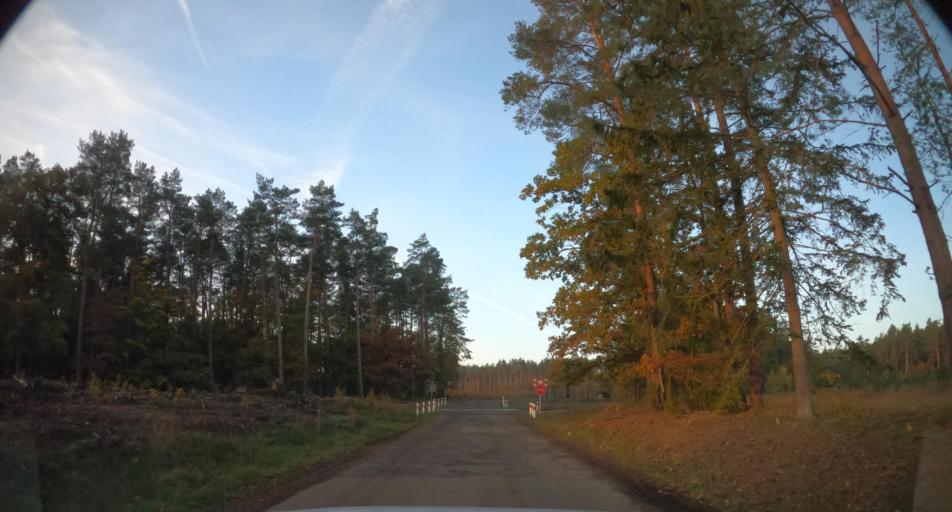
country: PL
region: West Pomeranian Voivodeship
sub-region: Powiat policki
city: Police
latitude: 53.6536
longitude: 14.4719
